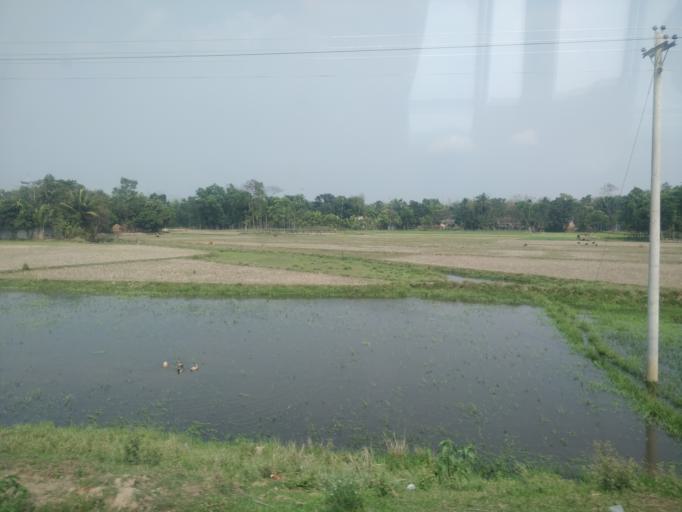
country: BD
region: Sylhet
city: Habiganj
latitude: 24.3234
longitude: 91.4338
